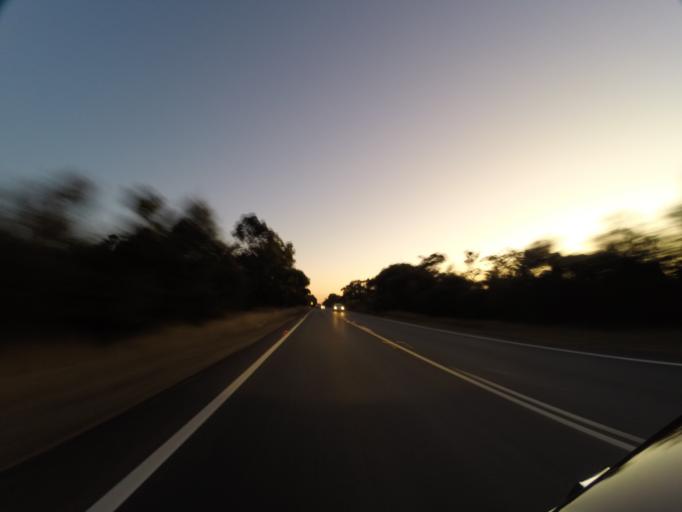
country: AU
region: New South Wales
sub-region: Sutherland Shire
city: Menai
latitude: -34.0174
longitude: 150.9804
